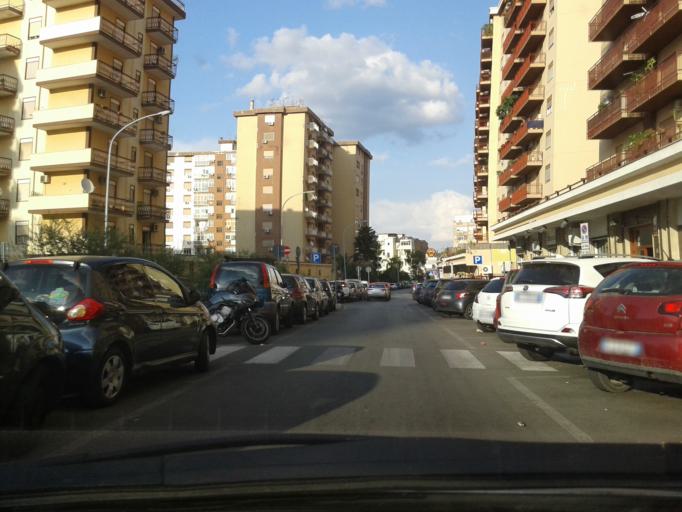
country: IT
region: Sicily
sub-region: Palermo
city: Palermo
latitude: 38.1069
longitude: 13.3375
